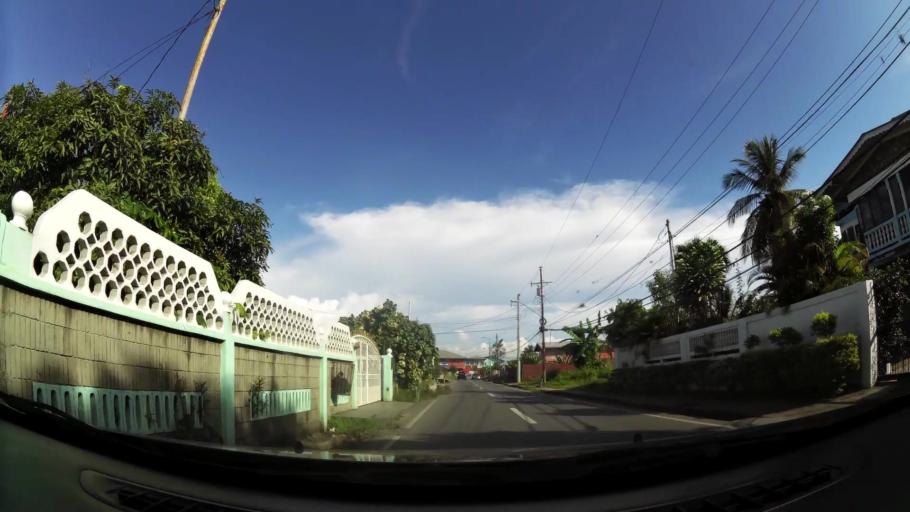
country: TT
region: Chaguanas
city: Chaguanas
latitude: 10.5314
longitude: -61.3790
